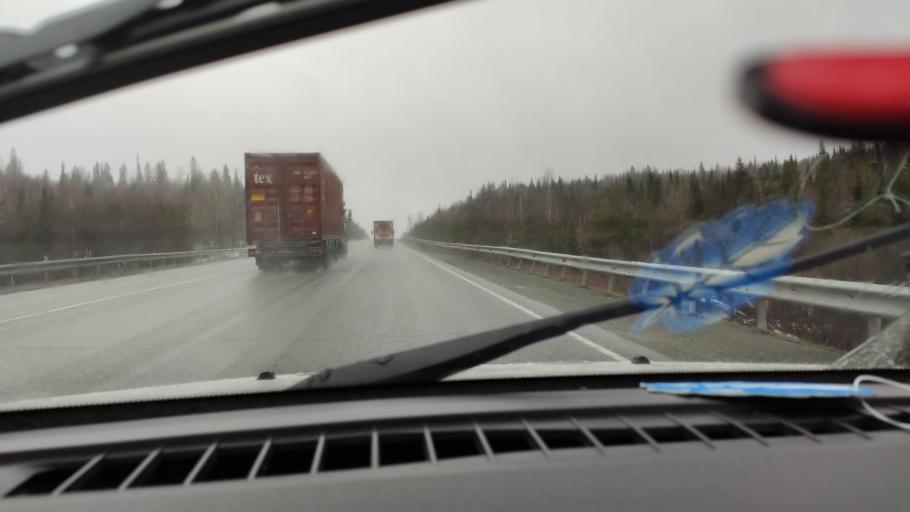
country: RU
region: Sverdlovsk
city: Arti
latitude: 56.7887
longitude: 58.5591
